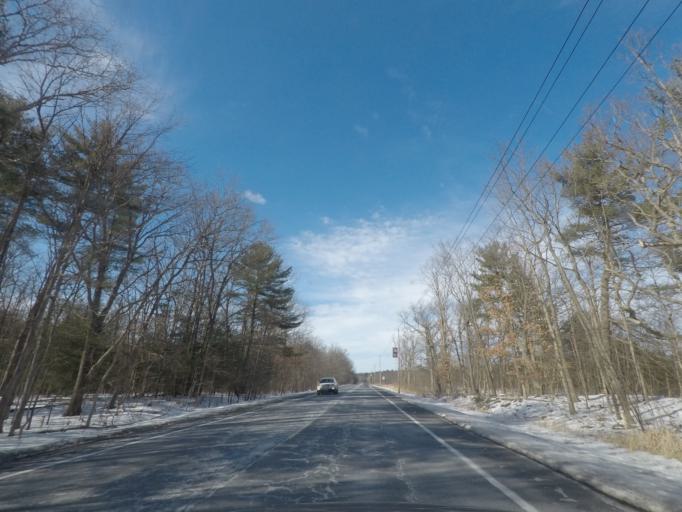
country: US
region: New York
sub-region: Albany County
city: Altamont
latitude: 42.7006
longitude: -73.9729
